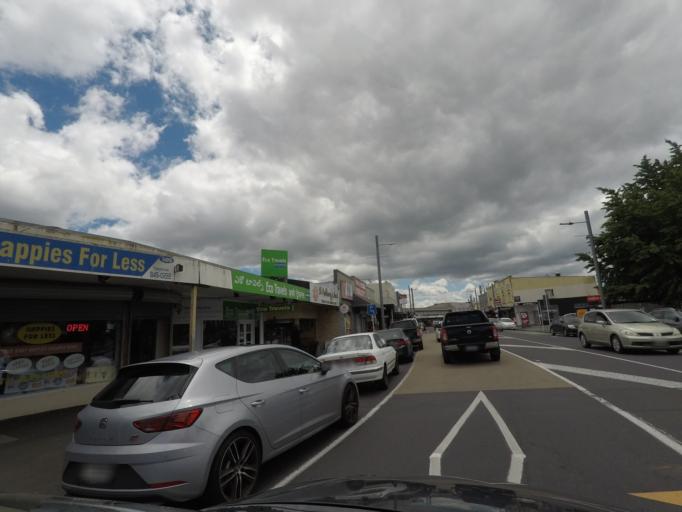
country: NZ
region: Auckland
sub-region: Auckland
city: Auckland
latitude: -36.8929
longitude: 174.7365
